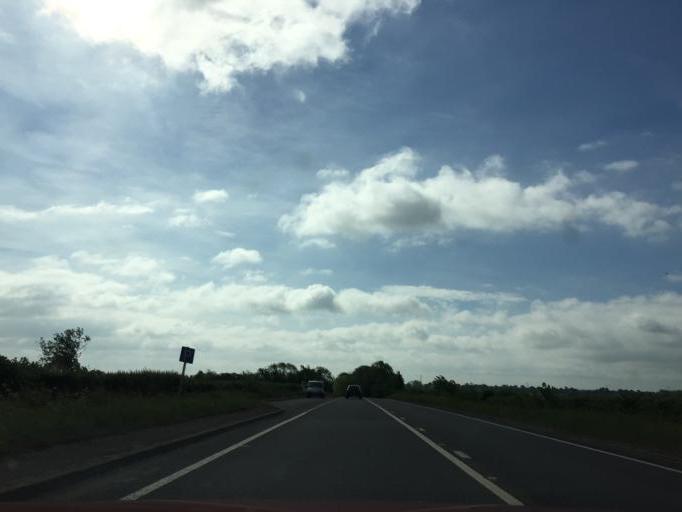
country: GB
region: England
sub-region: Northamptonshire
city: Towcester
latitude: 52.1159
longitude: -0.9603
